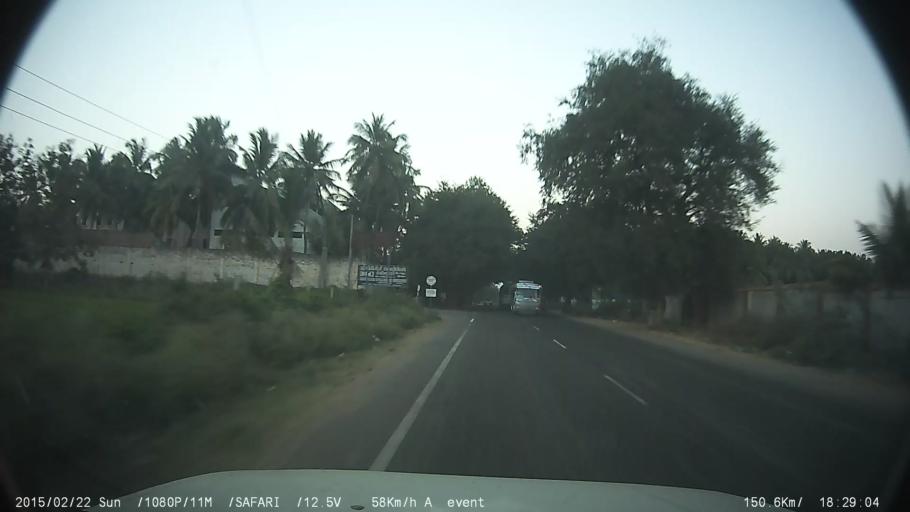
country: IN
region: Tamil Nadu
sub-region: Theni
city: Teni
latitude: 9.9820
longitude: 77.4523
